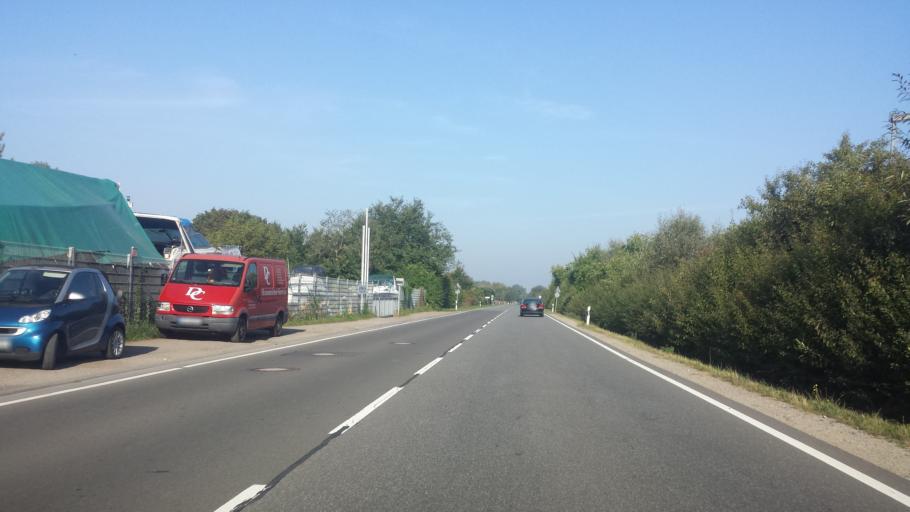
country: DE
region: Hesse
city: Lampertheim
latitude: 49.6128
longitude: 8.4434
